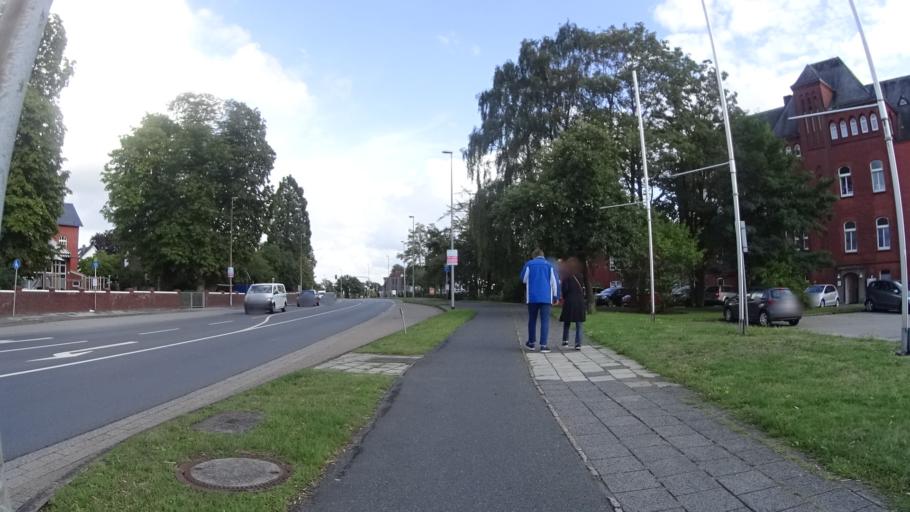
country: DE
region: Lower Saxony
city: Varel
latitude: 53.3931
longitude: 8.1405
